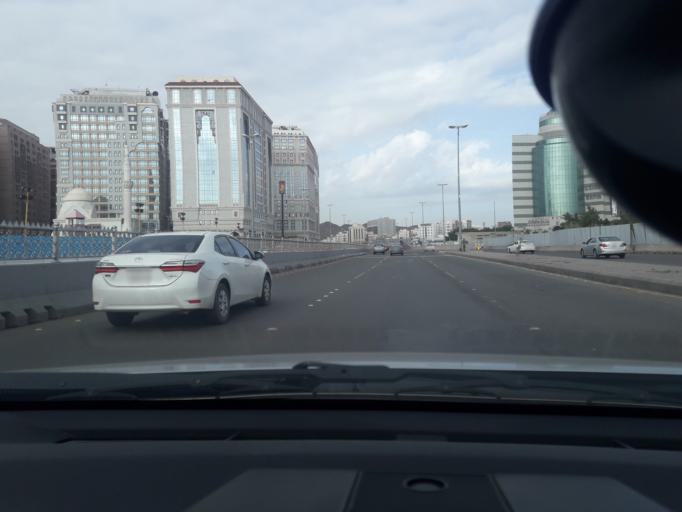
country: SA
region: Al Madinah al Munawwarah
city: Medina
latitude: 24.4733
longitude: 39.6156
